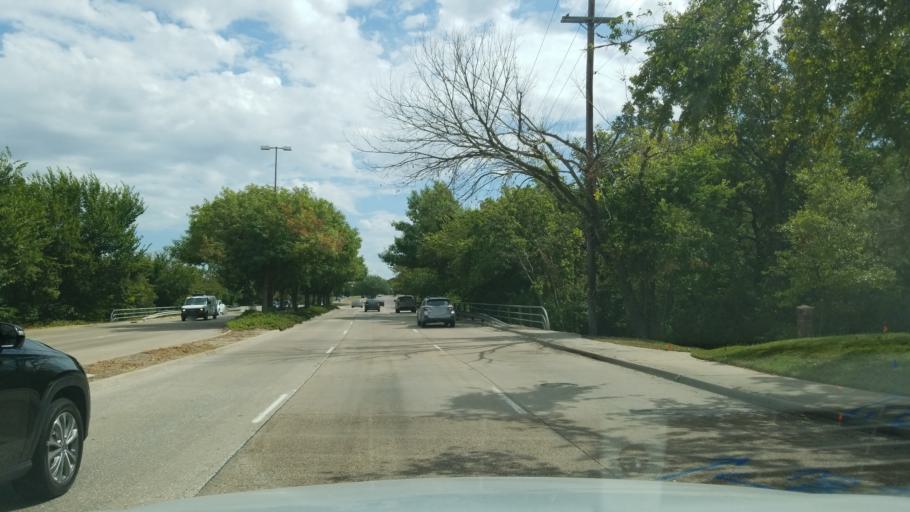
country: US
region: Texas
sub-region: Dallas County
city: Addison
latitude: 32.9540
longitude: -96.8105
